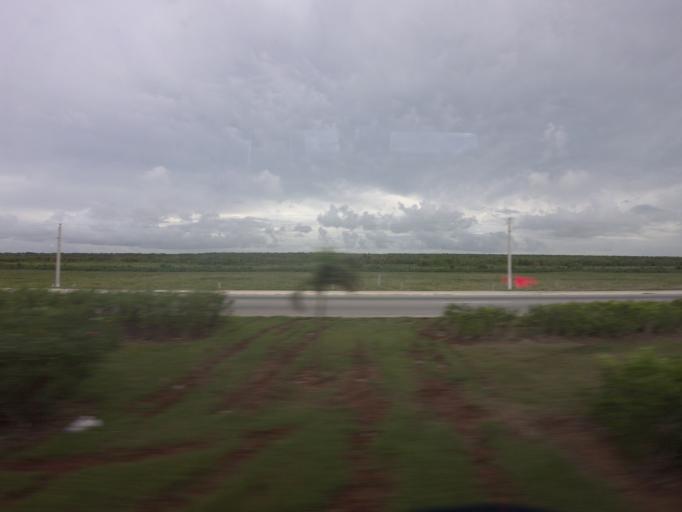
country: CU
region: Matanzas
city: Varadero
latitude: 23.1083
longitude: -81.3861
